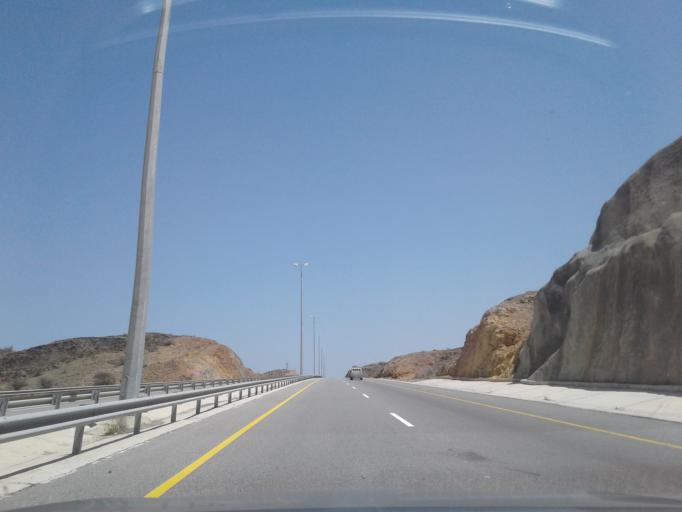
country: OM
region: Muhafazat Masqat
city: Muscat
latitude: 23.2068
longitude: 58.8106
